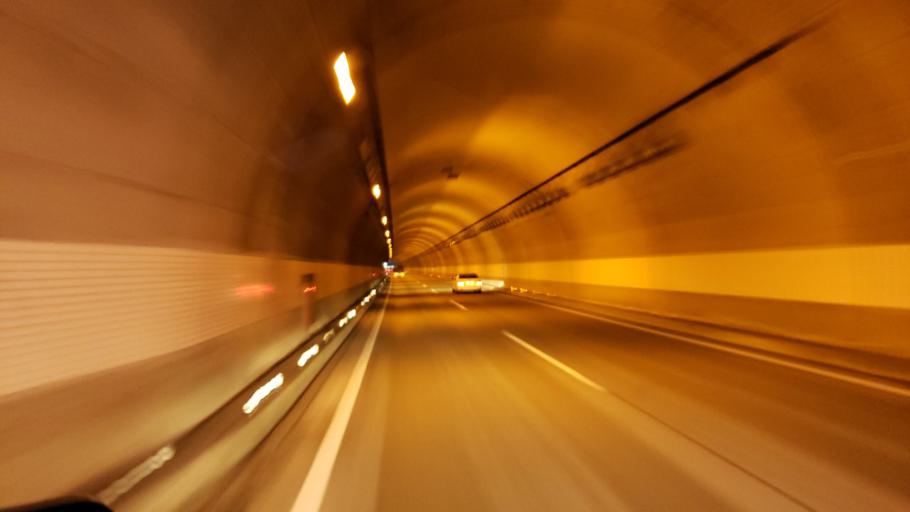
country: JP
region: Hyogo
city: Himeji
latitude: 34.8532
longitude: 134.7708
